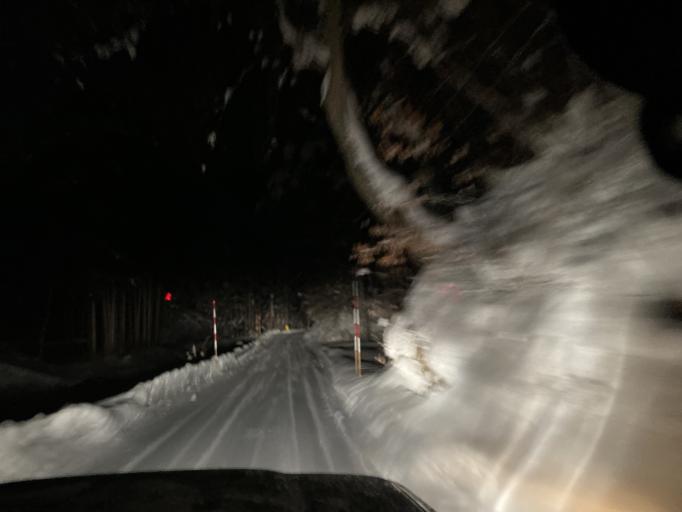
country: JP
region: Nagano
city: Omachi
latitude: 36.5599
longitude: 137.8603
